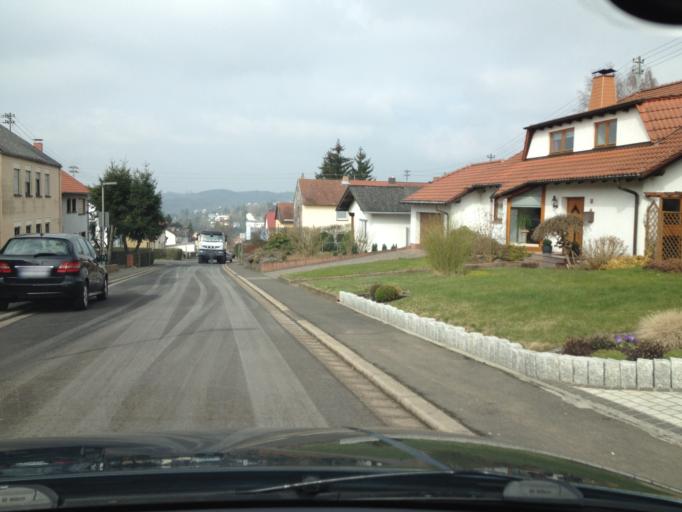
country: DE
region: Saarland
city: Ottweiler
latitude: 49.4031
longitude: 7.1756
